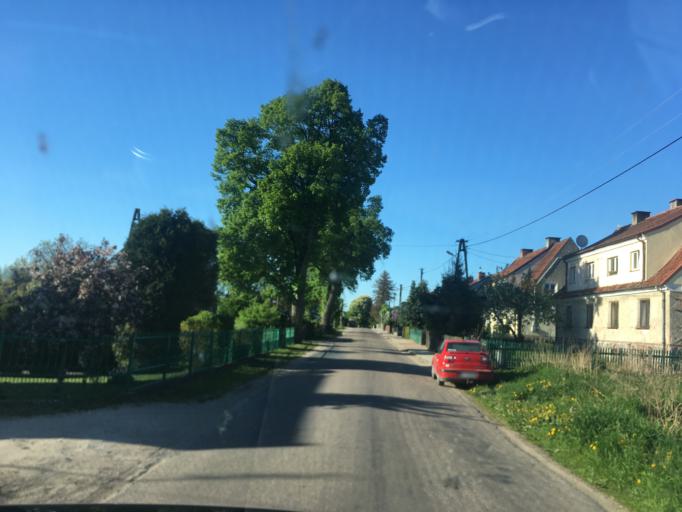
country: PL
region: Warmian-Masurian Voivodeship
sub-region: Powiat piski
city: Ruciane-Nida
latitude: 53.6840
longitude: 21.4994
